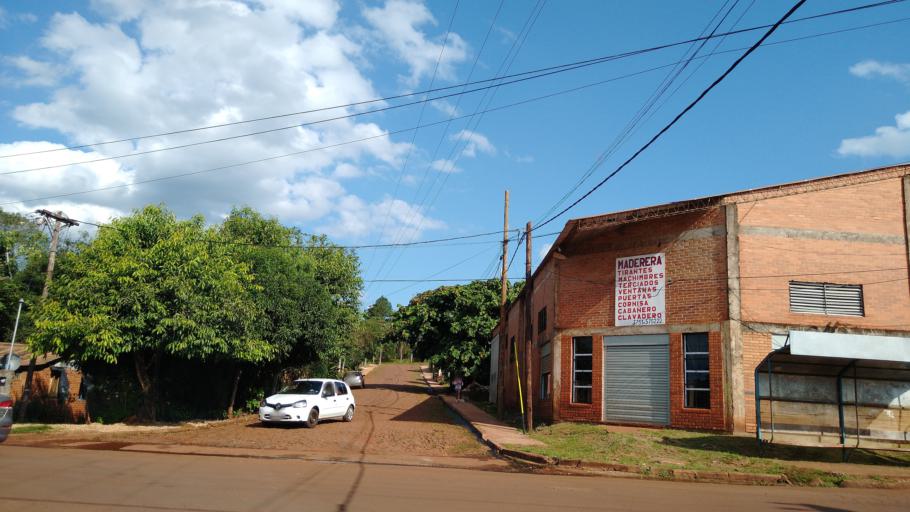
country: AR
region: Misiones
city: Puerto Piray
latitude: -26.4685
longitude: -54.7073
